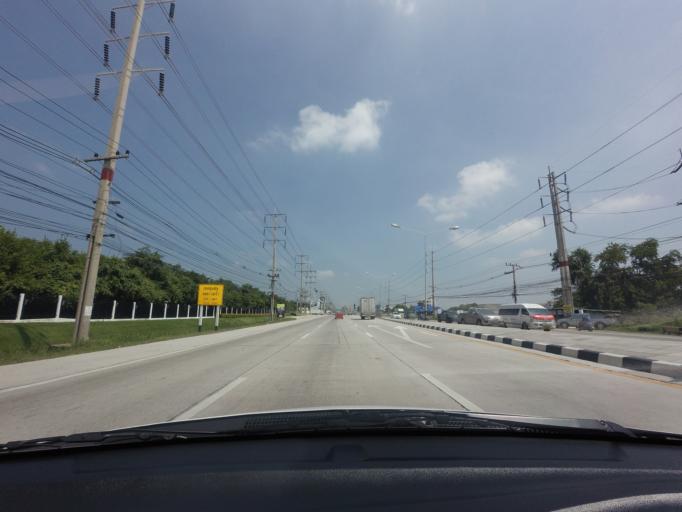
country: TH
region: Chachoengsao
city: Ban Pho
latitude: 13.6145
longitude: 101.0272
